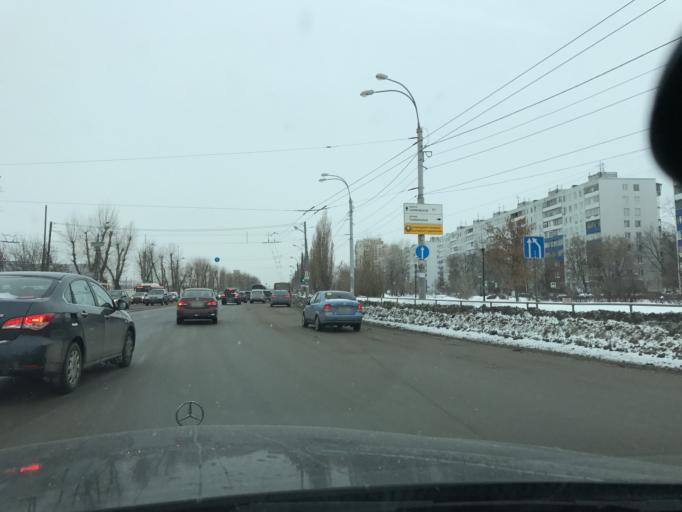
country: RU
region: Nizjnij Novgorod
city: Nizhniy Novgorod
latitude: 56.3221
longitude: 43.9411
